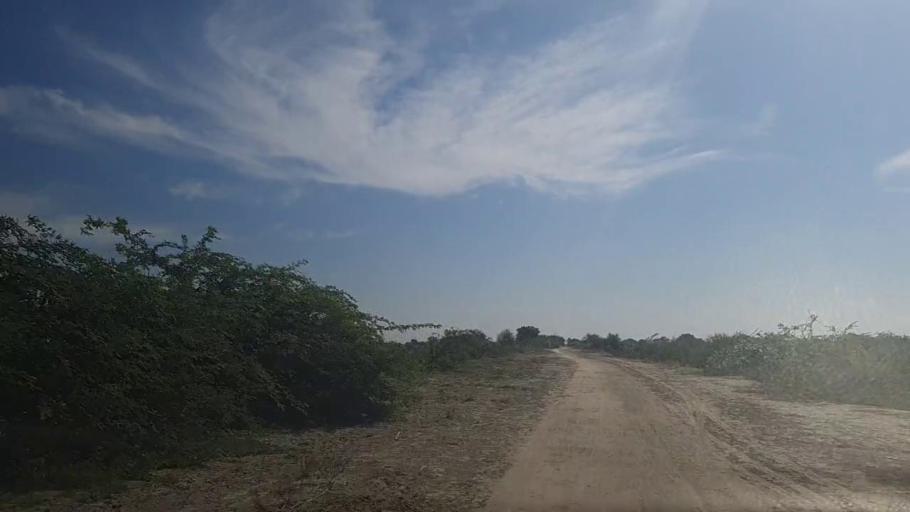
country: PK
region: Sindh
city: Mirpur Batoro
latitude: 24.6583
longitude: 68.1964
